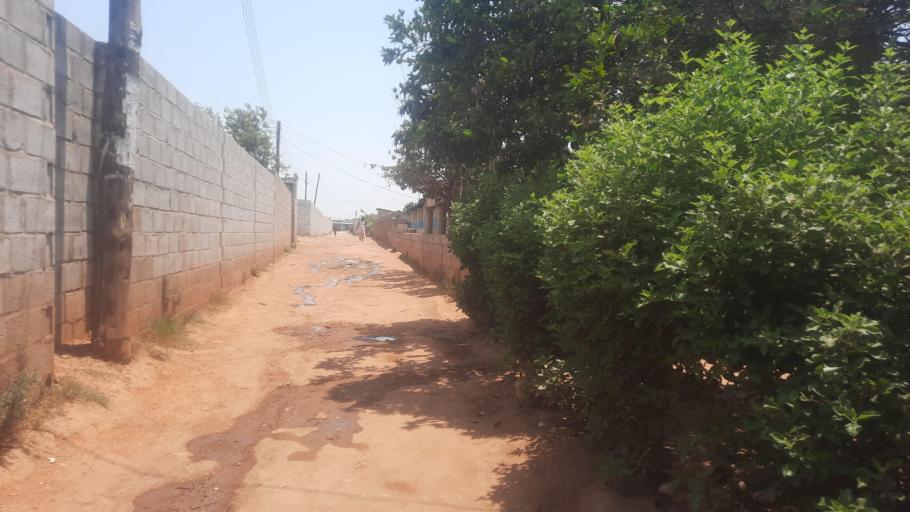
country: ZM
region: Lusaka
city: Lusaka
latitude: -15.4016
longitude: 28.3723
